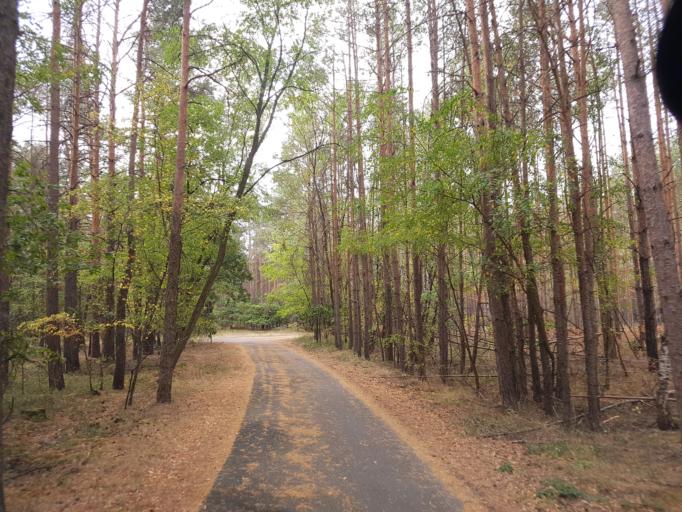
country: DE
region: Brandenburg
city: Finsterwalde
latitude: 51.5999
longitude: 13.7596
